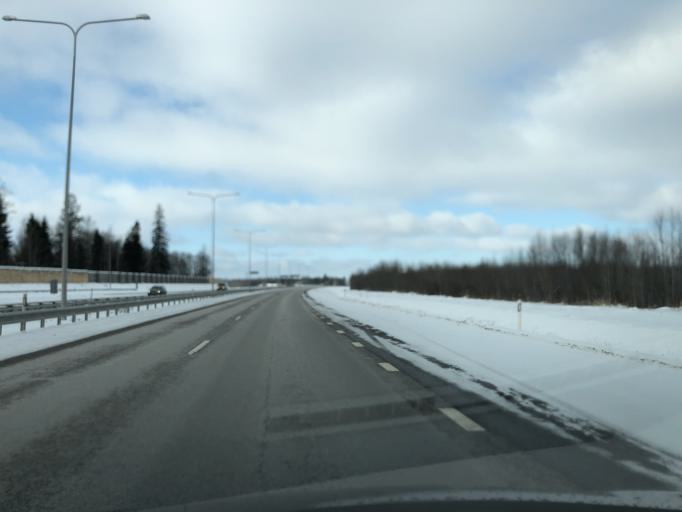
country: EE
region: Jaervamaa
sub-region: Paide linn
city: Paide
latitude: 58.9018
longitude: 25.6368
